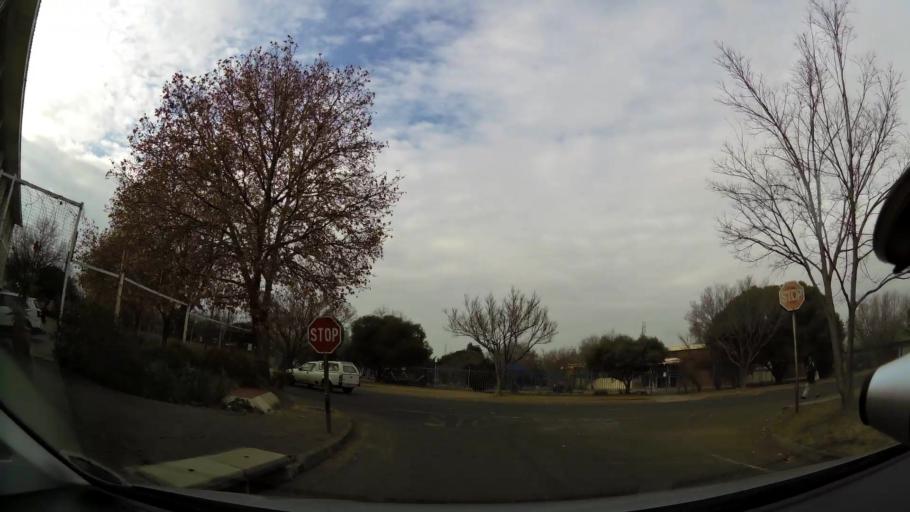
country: ZA
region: Orange Free State
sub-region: Mangaung Metropolitan Municipality
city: Bloemfontein
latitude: -29.1210
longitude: 26.1907
